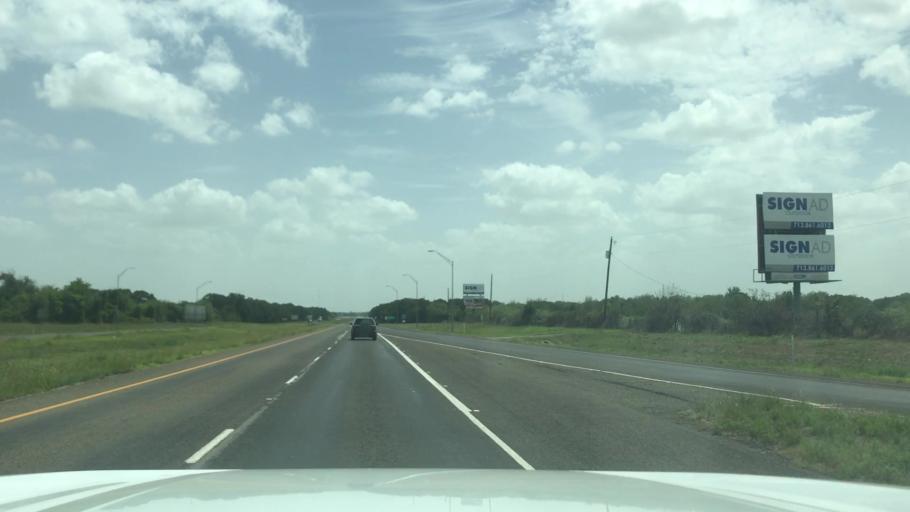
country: US
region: Texas
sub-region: Falls County
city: Marlin
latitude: 31.3017
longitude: -96.8749
